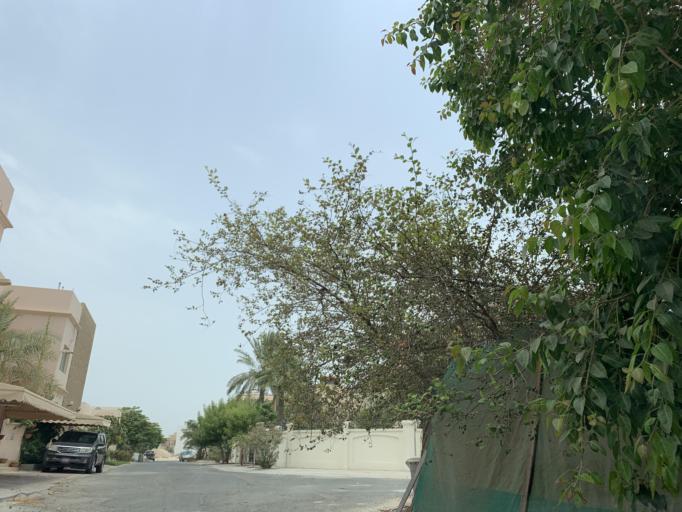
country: BH
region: Northern
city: Madinat `Isa
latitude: 26.1879
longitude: 50.4725
